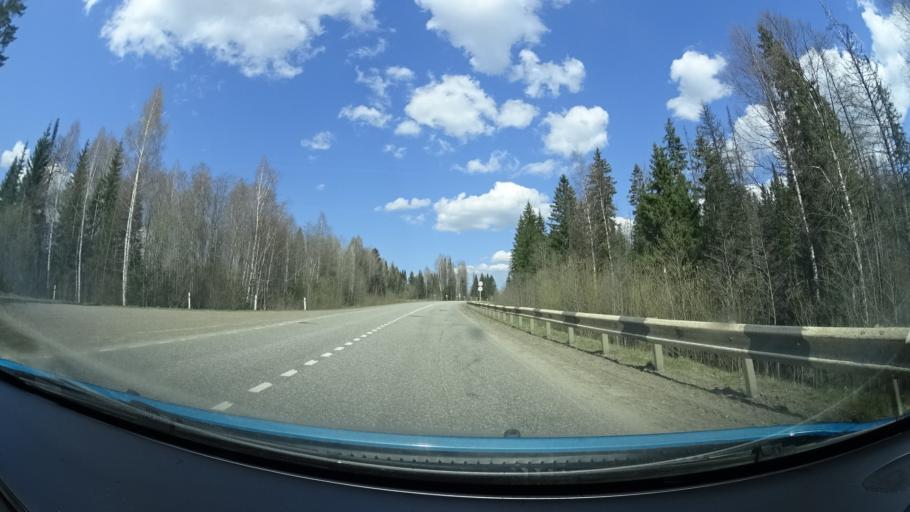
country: RU
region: Perm
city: Osa
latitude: 57.3884
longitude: 55.6086
